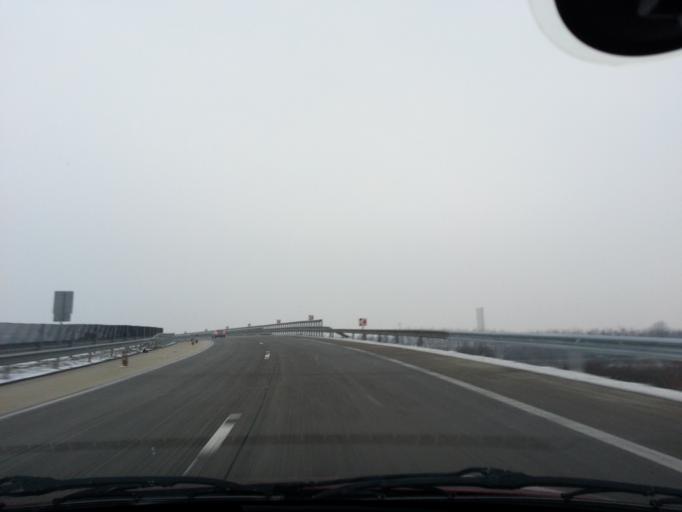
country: HU
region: Pest
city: Nagytarcsa
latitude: 47.5101
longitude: 19.2959
